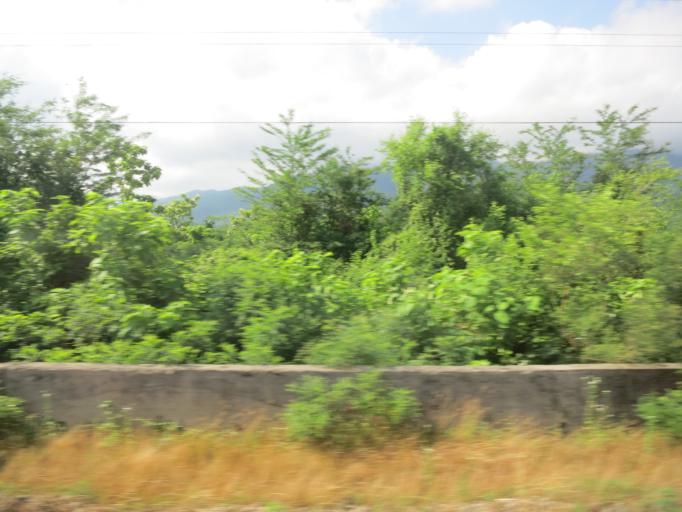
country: GE
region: Imereti
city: Samtredia
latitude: 42.0964
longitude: 42.2396
